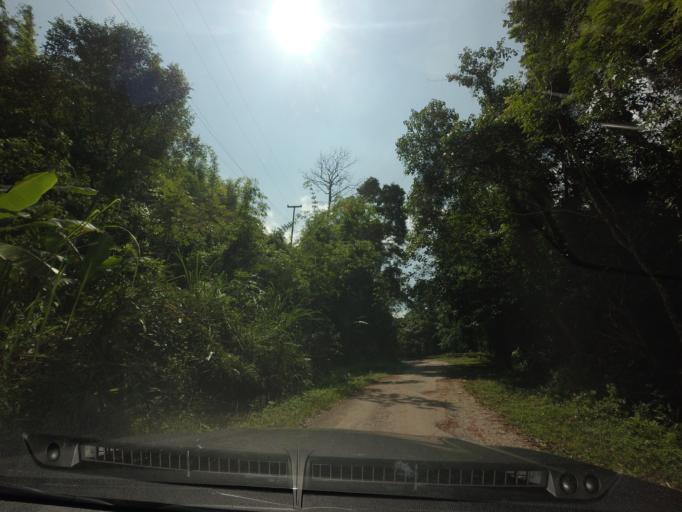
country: TH
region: Loei
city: Na Haeo
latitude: 17.5204
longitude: 100.9381
